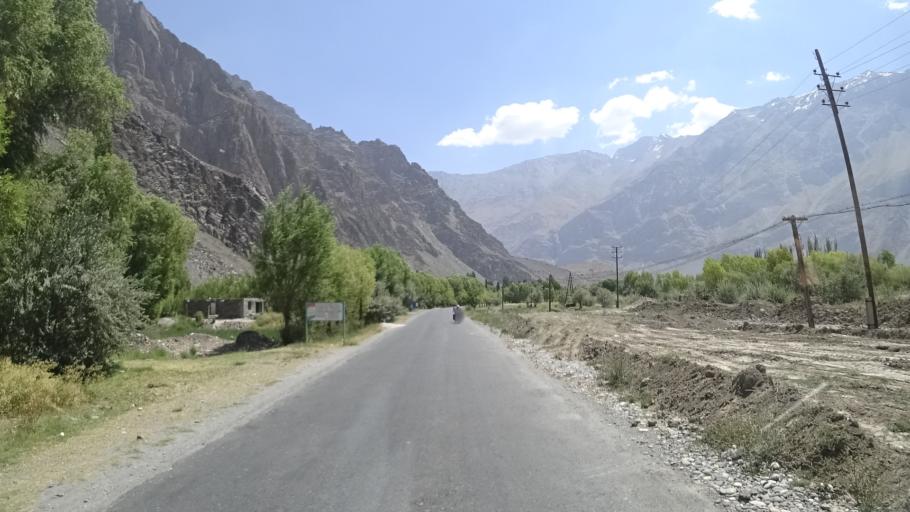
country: TJ
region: Gorno-Badakhshan
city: Rushon
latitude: 37.9469
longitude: 71.5707
